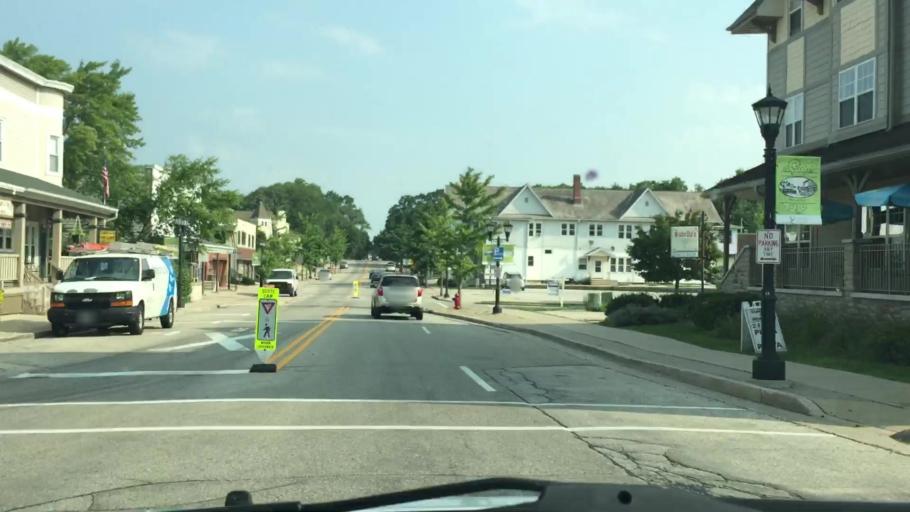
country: US
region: Wisconsin
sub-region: Waukesha County
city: Brookfield
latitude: 43.0719
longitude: -88.1459
